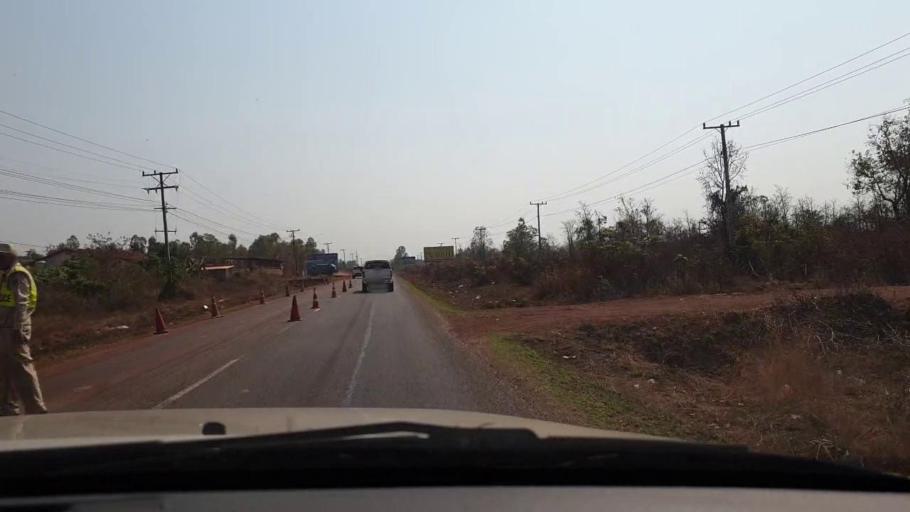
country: TH
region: Nong Khai
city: Nong Khai
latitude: 18.0531
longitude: 102.8437
